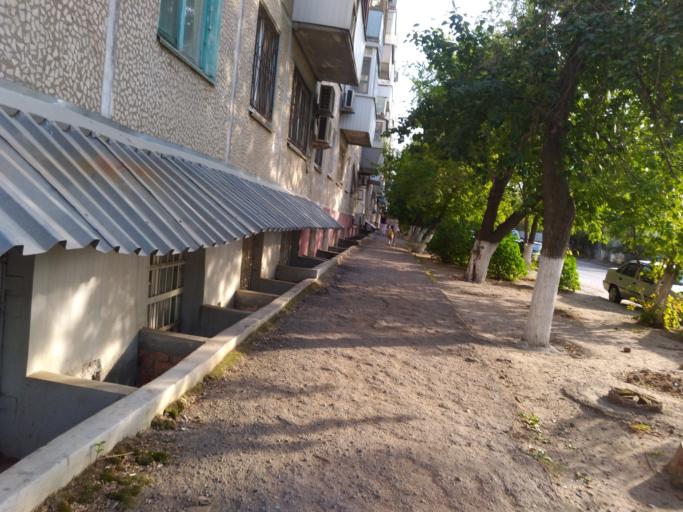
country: RU
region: Volgograd
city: Volgograd
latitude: 48.7000
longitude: 44.4990
